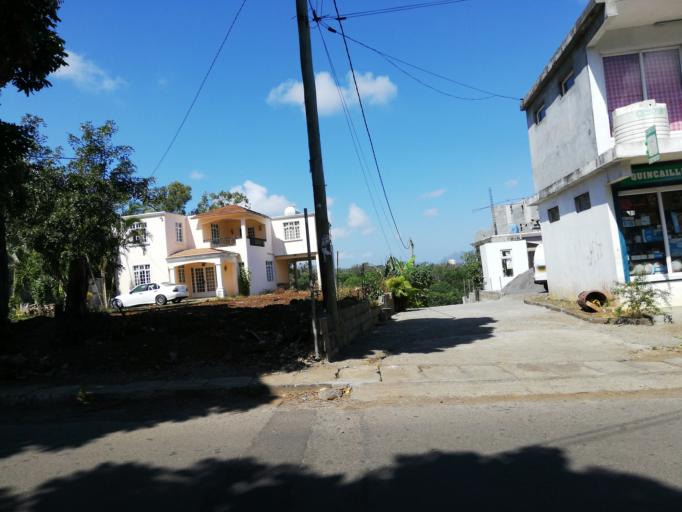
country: MU
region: Moka
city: Moka
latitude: -20.2179
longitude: 57.4891
